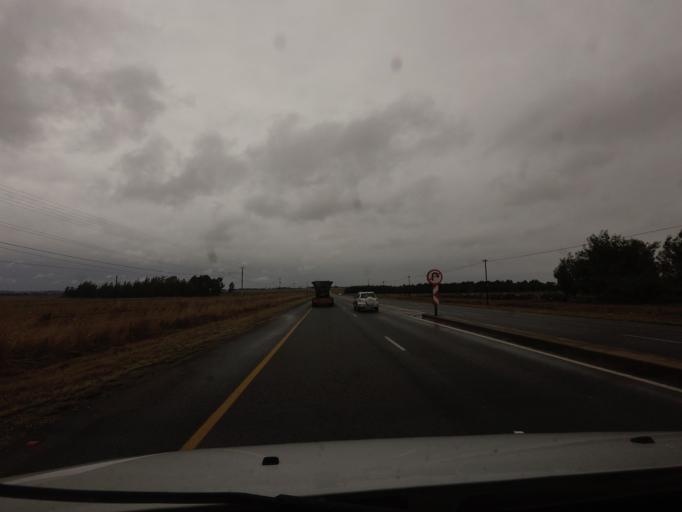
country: ZA
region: Mpumalanga
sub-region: Nkangala District Municipality
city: Belfast
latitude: -25.7287
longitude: 30.0248
